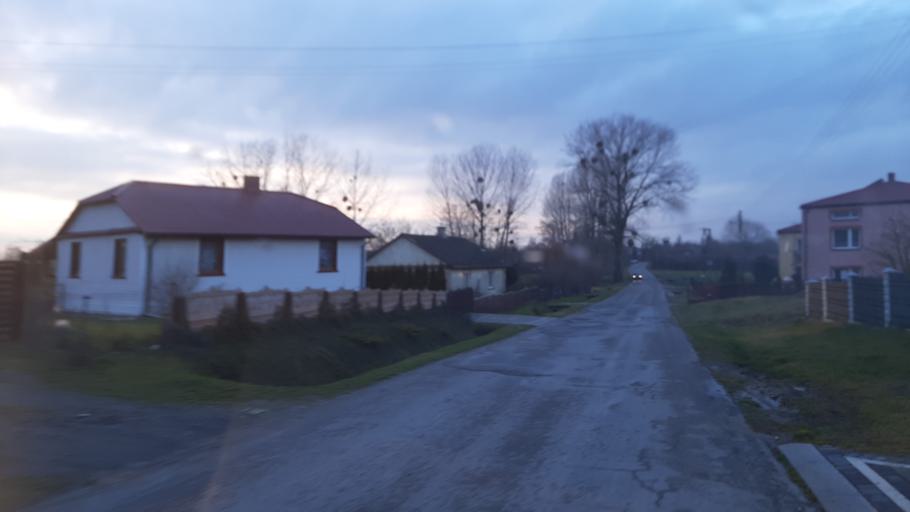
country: PL
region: Lublin Voivodeship
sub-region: Powiat lubelski
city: Garbow
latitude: 51.3814
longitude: 22.3922
